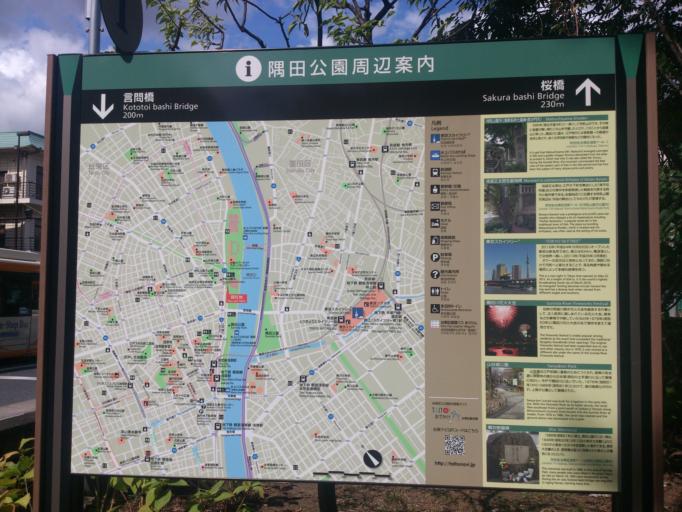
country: JP
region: Tokyo
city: Urayasu
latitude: 35.7165
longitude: 139.8032
